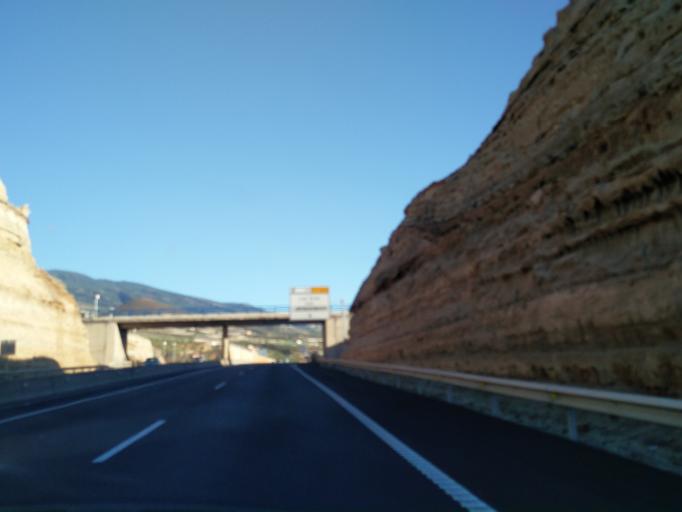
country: ES
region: Canary Islands
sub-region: Provincia de Santa Cruz de Tenerife
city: Fasnia
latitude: 28.1997
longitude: -16.4262
